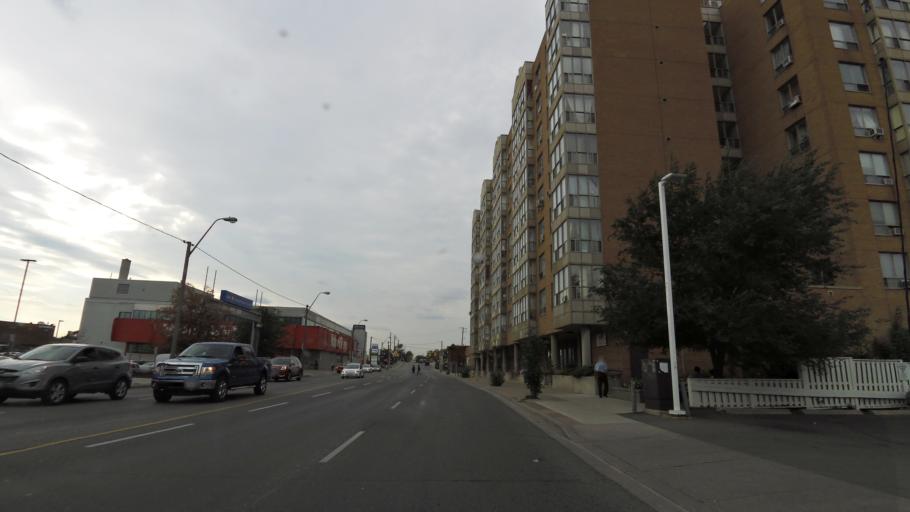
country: CA
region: Ontario
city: Toronto
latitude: 43.6820
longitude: -79.4720
